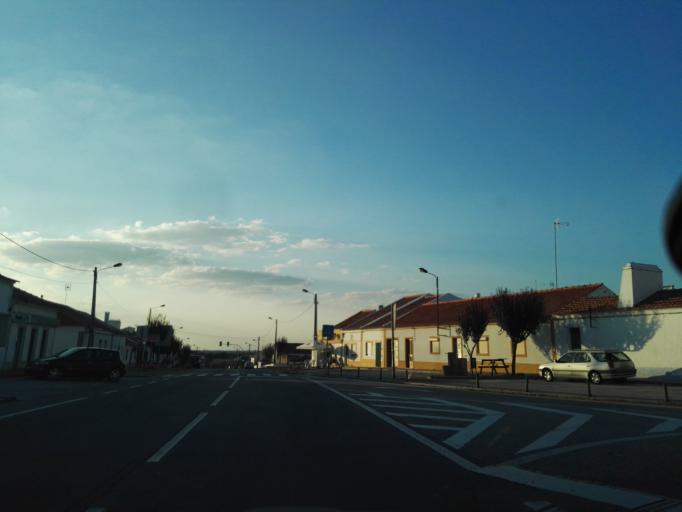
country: PT
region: Evora
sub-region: Mora
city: Mora
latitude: 38.8946
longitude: -8.0212
